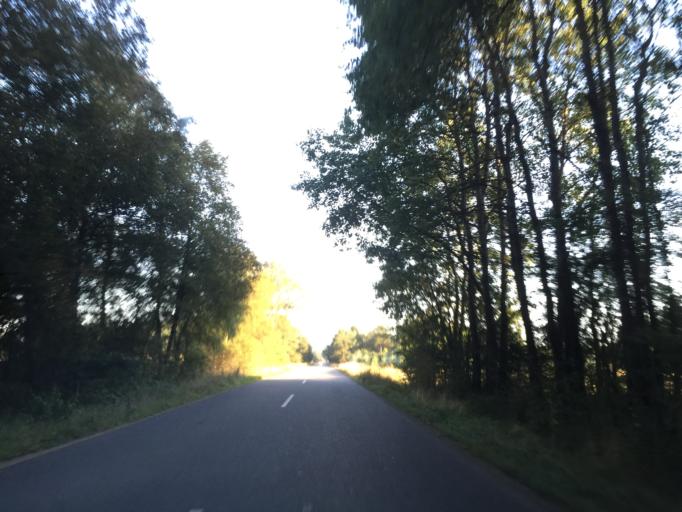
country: DK
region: Central Jutland
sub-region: Viborg Kommune
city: Bjerringbro
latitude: 56.2917
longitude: 9.6745
